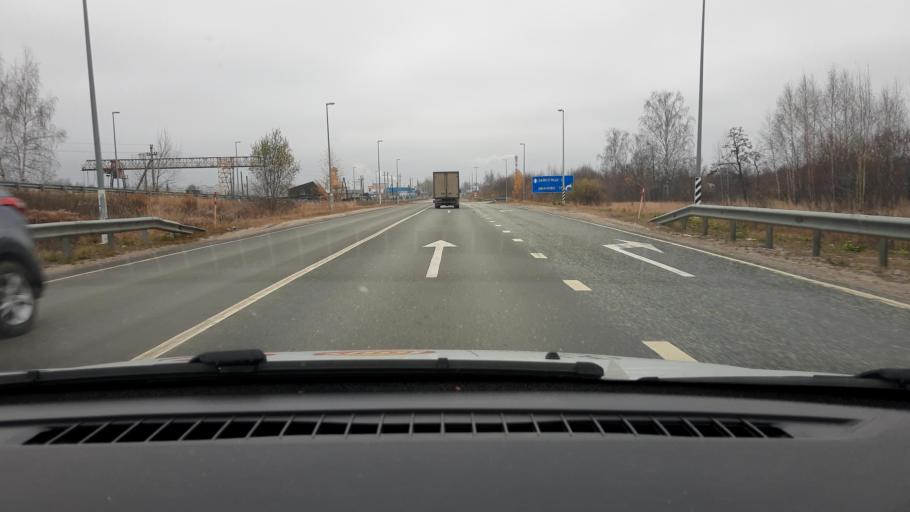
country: RU
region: Nizjnij Novgorod
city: Zavolzh'ye
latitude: 56.6183
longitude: 43.4321
